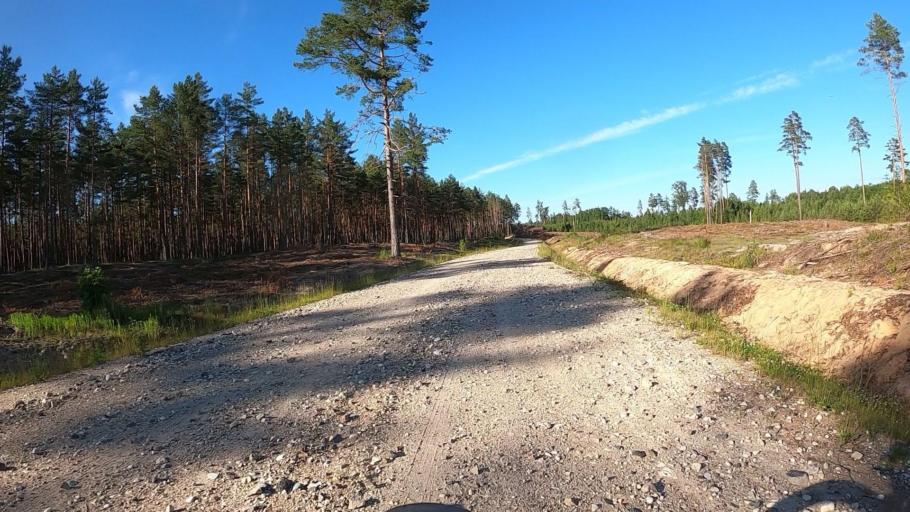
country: LV
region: Carnikava
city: Carnikava
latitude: 57.1071
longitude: 24.2500
